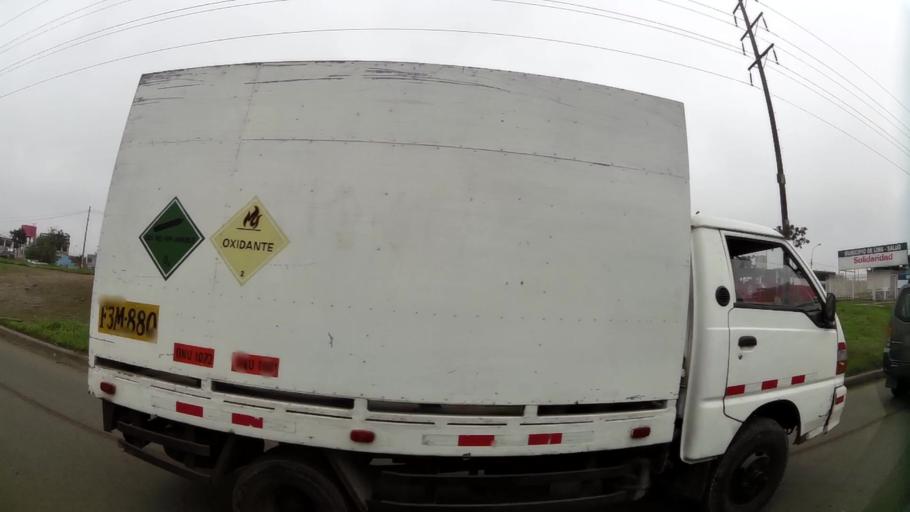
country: PE
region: Lima
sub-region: Lima
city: Surco
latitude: -12.1734
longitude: -76.9450
